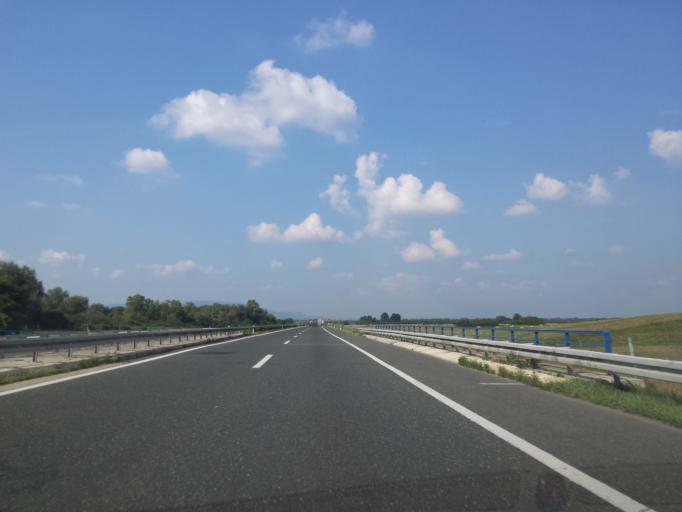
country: HR
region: Zagrebacka
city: Jastrebarsko
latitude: 45.5934
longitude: 15.6307
